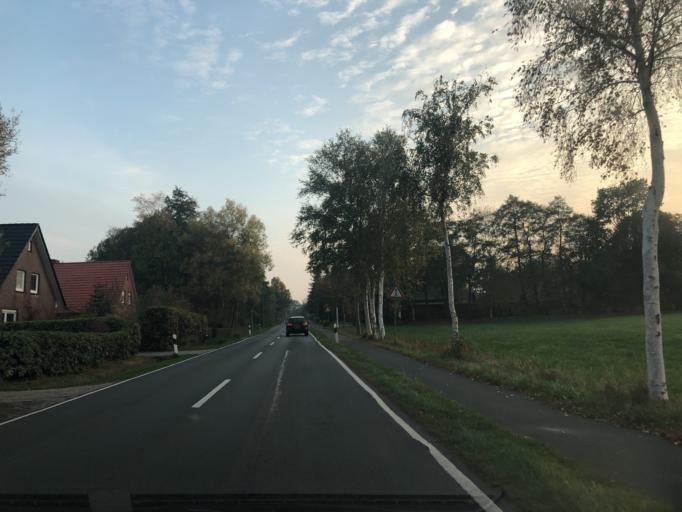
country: DE
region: Lower Saxony
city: Wardenburg
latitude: 53.0690
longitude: 8.1642
